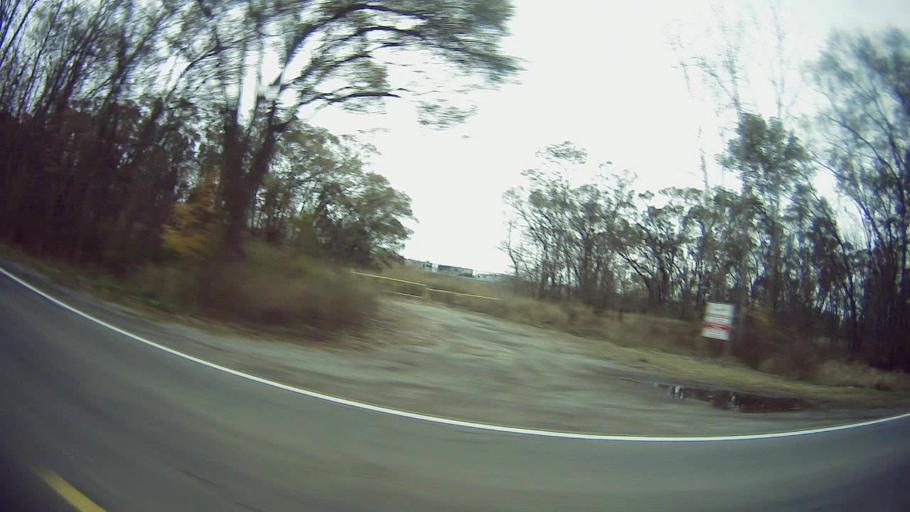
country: US
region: Michigan
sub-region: Macomb County
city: Sterling Heights
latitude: 42.5421
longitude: -83.0041
